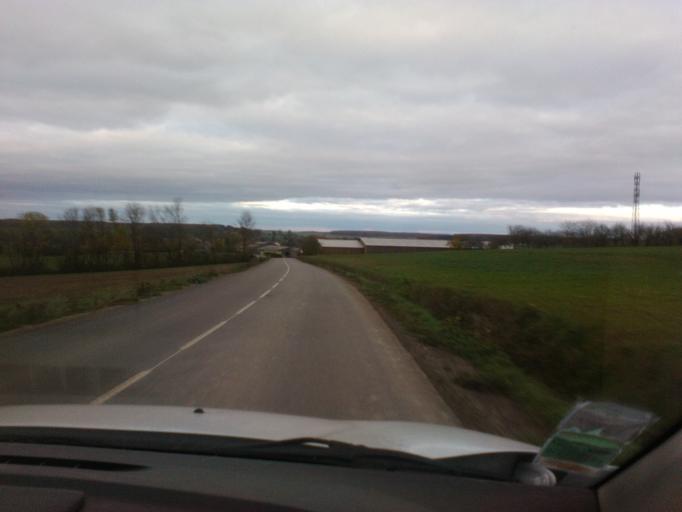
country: FR
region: Lorraine
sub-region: Departement des Vosges
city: Darnieulles
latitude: 48.2367
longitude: 6.3295
